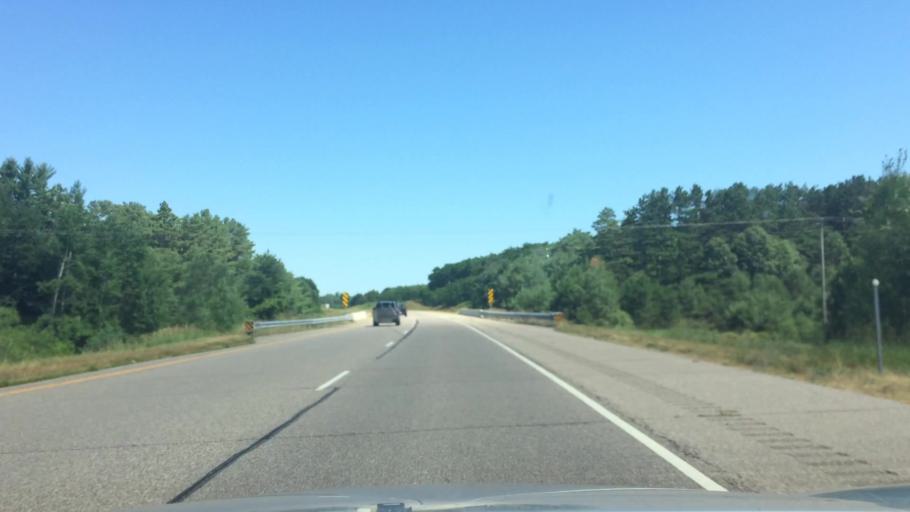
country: US
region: Wisconsin
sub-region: Marquette County
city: Westfield
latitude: 44.0819
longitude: -89.5323
